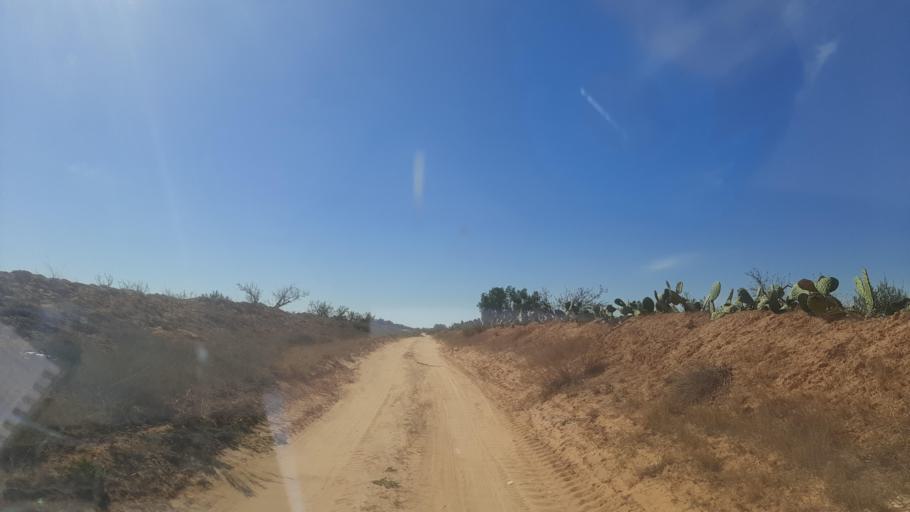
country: TN
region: Safaqis
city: Sfax
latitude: 34.8271
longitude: 10.5548
